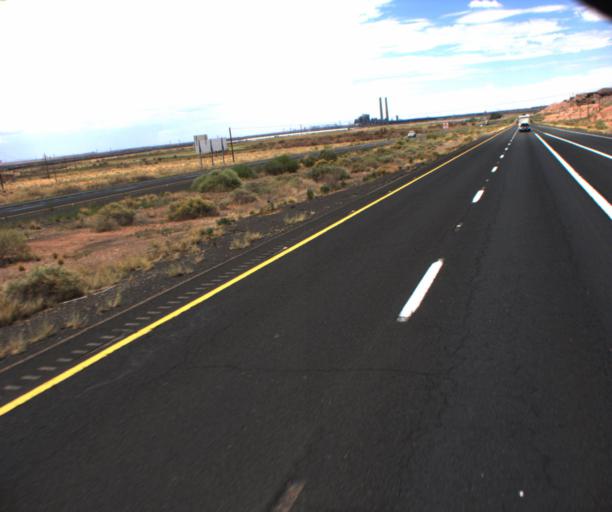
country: US
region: Arizona
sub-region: Navajo County
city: Joseph City
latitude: 34.9245
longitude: -110.2626
